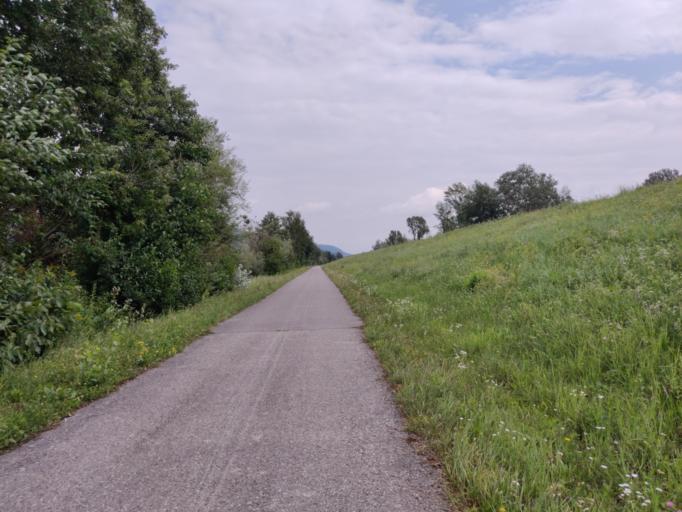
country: AT
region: Lower Austria
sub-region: Politischer Bezirk Melk
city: Marbach an der Donau
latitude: 48.2125
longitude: 15.1678
